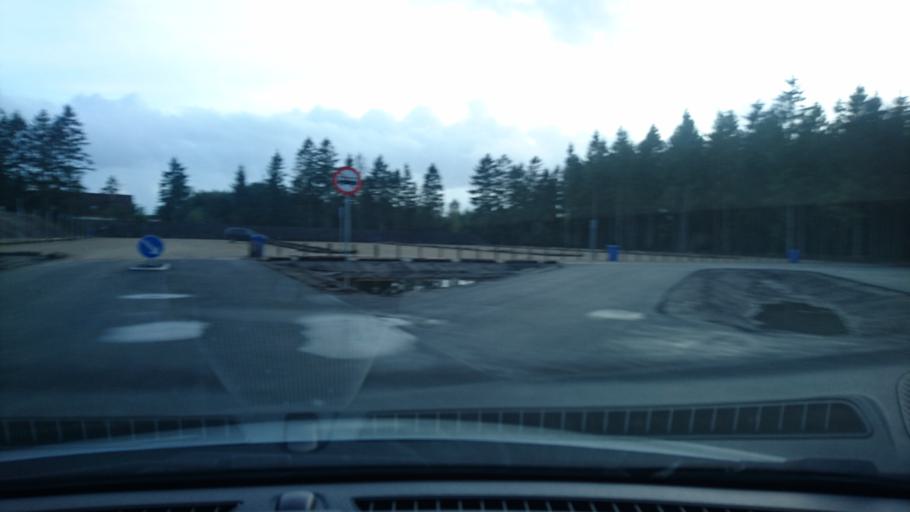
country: DK
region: South Denmark
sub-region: Billund Kommune
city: Billund
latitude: 55.7379
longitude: 9.1116
